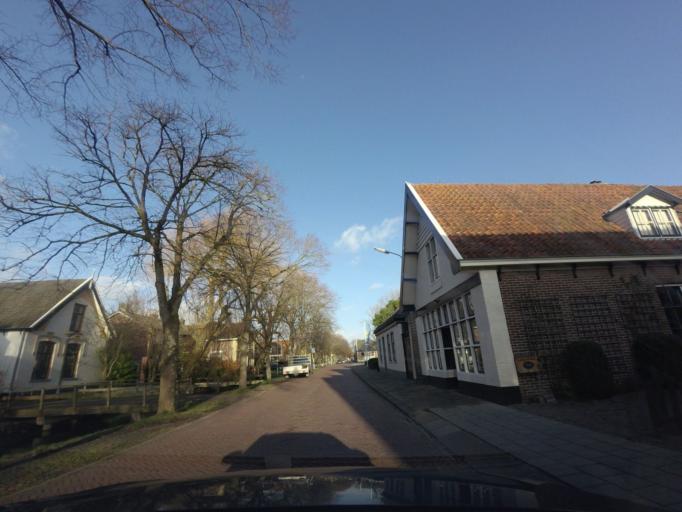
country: NL
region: North Holland
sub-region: Gemeente Opmeer
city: Opmeer
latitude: 52.7372
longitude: 4.8931
